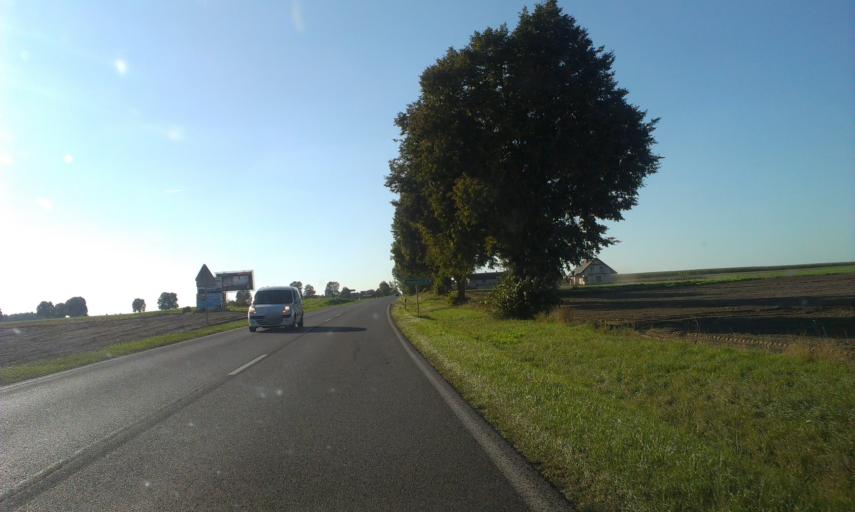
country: PL
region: Kujawsko-Pomorskie
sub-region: Powiat swiecki
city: Bukowiec
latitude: 53.4475
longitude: 18.2548
